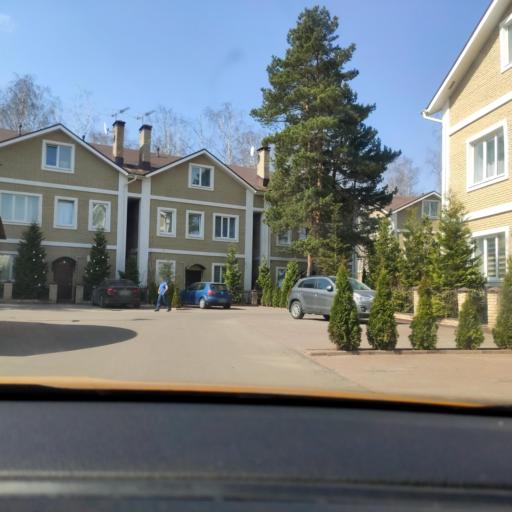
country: RU
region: Moskovskaya
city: Pavlovskaya Sloboda
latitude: 55.8115
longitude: 37.1047
